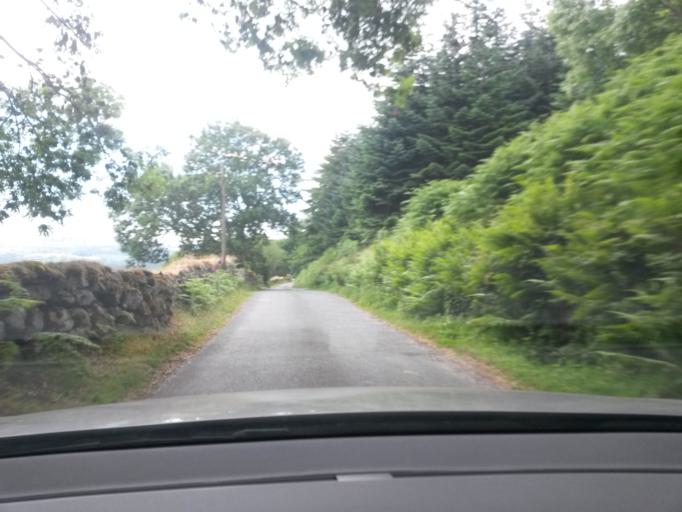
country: IE
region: Leinster
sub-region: Wicklow
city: Enniskerry
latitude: 53.1724
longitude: -6.2432
